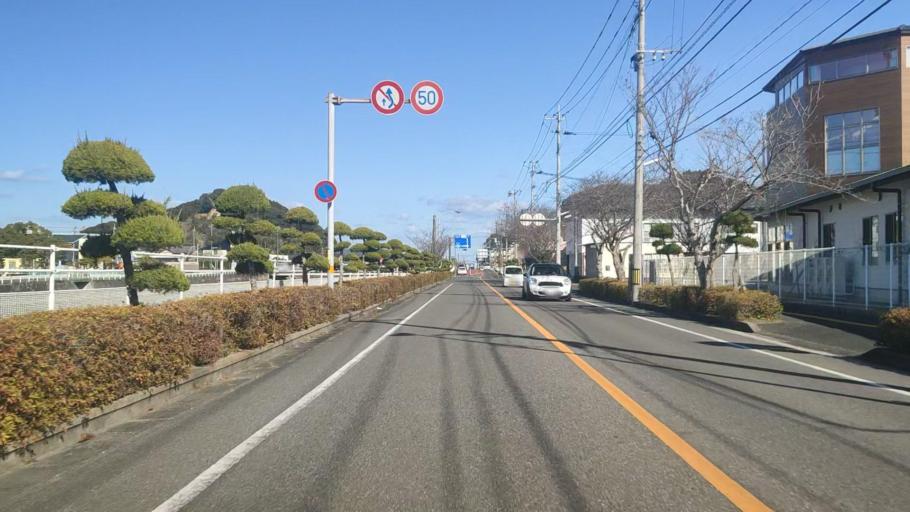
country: JP
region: Oita
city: Saiki
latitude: 32.9541
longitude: 131.9077
